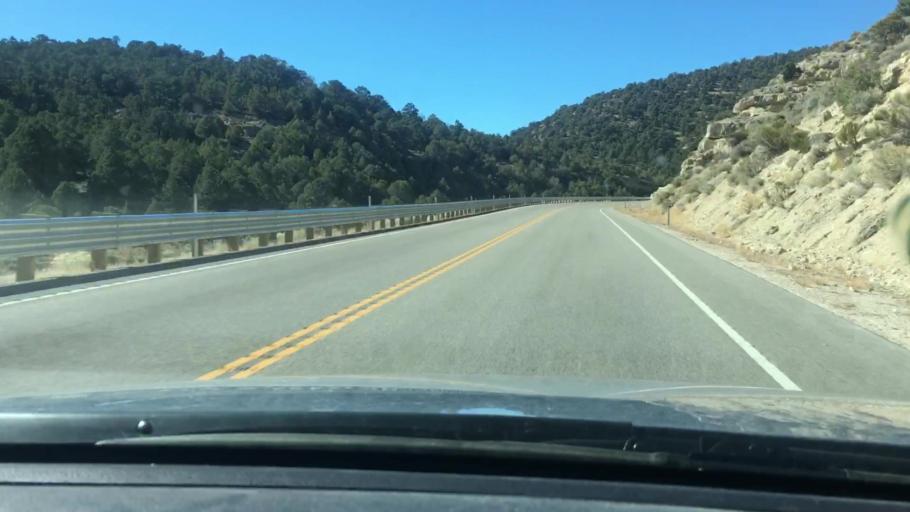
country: US
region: Nevada
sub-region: White Pine County
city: Ely
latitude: 39.2203
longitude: -114.9382
